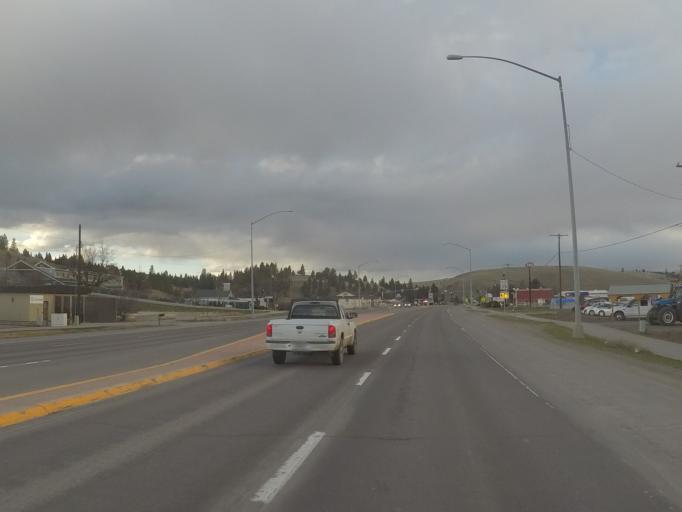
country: US
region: Montana
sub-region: Missoula County
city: Lolo
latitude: 46.7604
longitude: -114.0816
